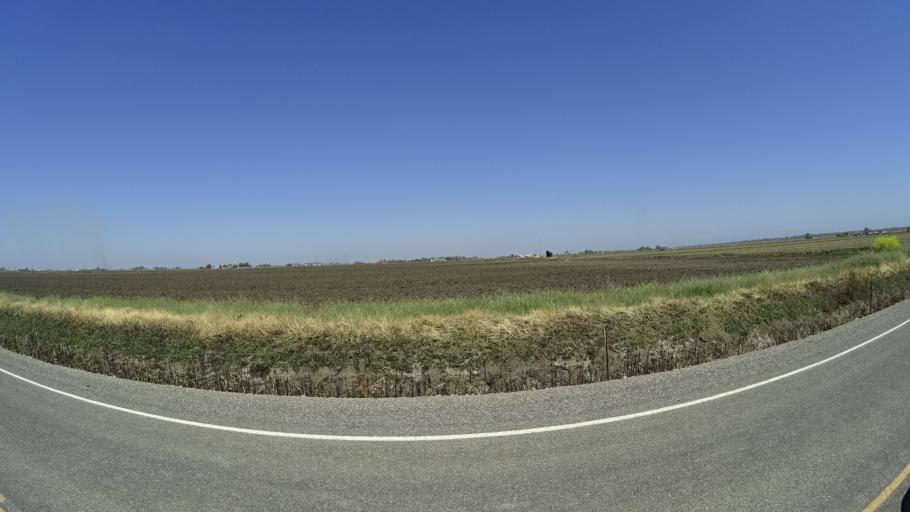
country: US
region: California
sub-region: Glenn County
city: Willows
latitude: 39.5580
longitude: -122.0382
